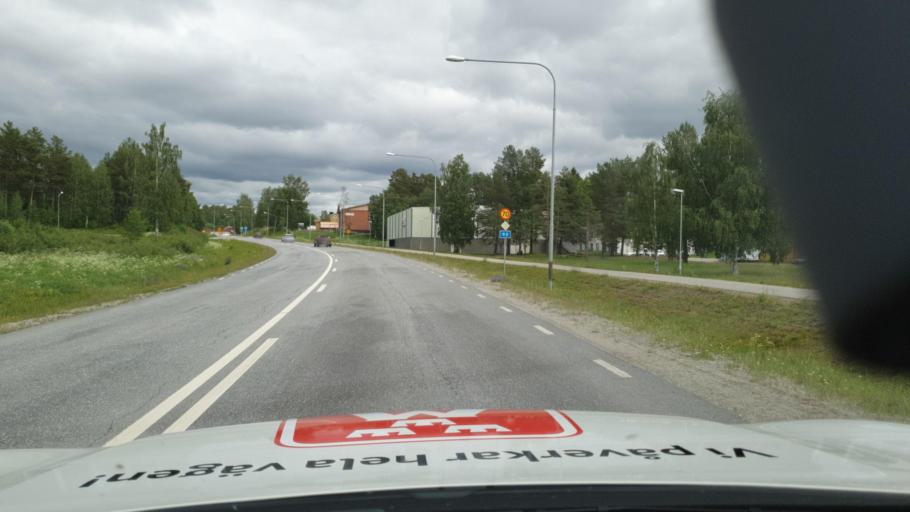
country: SE
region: Vaesterbotten
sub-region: Asele Kommun
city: Asele
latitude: 64.1610
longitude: 17.3381
